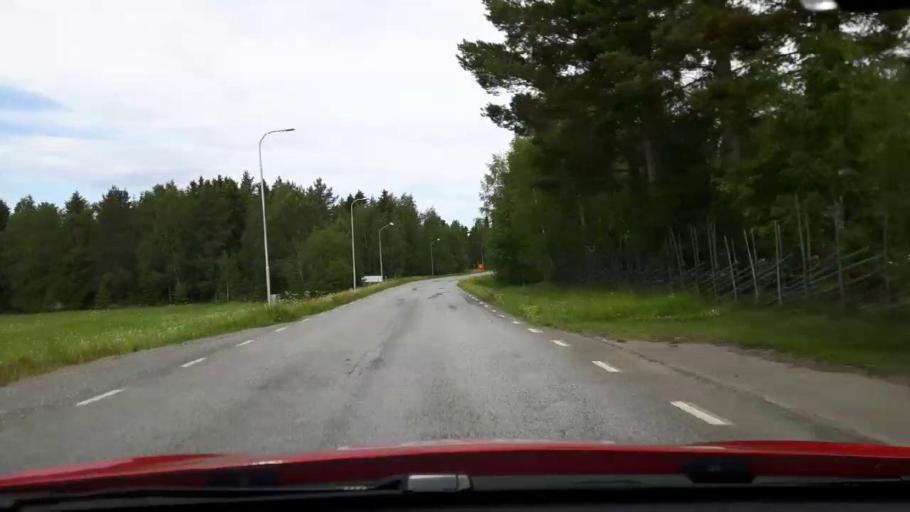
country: SE
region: Jaemtland
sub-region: Bergs Kommun
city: Hoverberg
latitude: 63.0240
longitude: 14.4761
